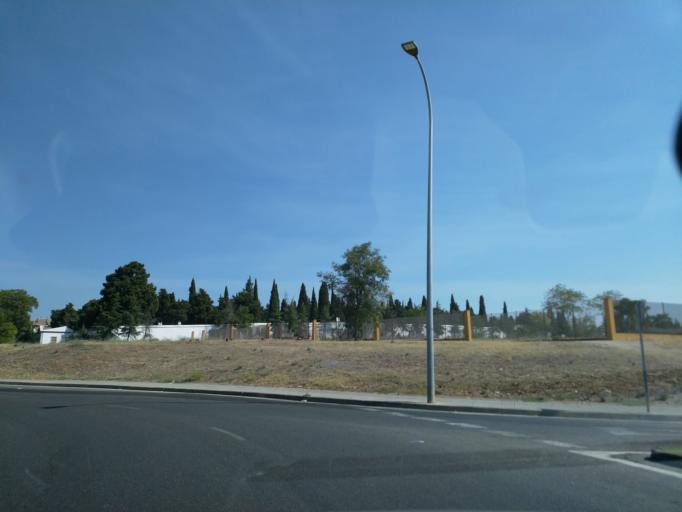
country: ES
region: Extremadura
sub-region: Provincia de Badajoz
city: Merida
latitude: 38.9298
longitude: -6.3472
